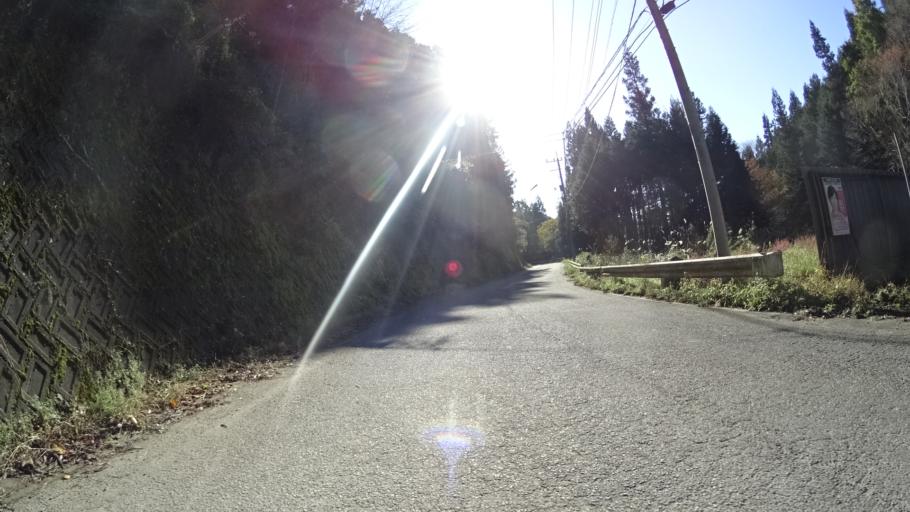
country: JP
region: Yamanashi
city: Uenohara
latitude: 35.6686
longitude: 139.1060
